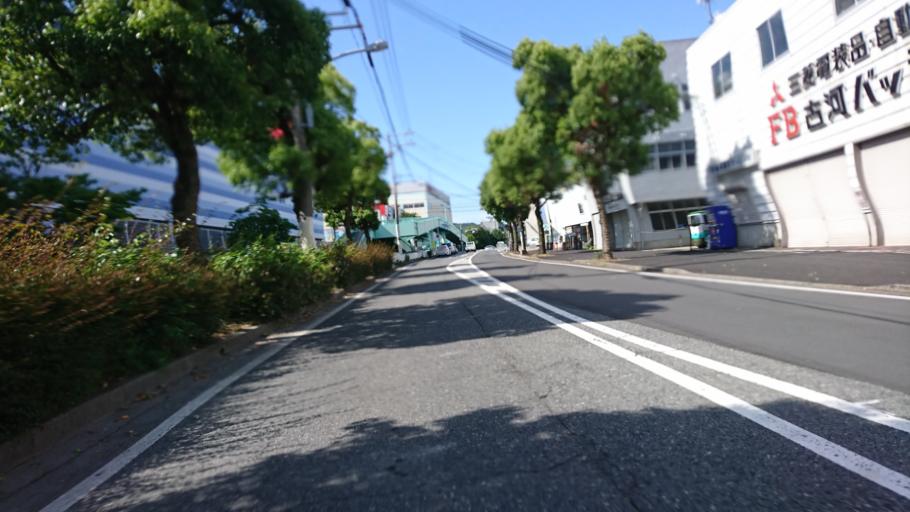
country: JP
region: Hyogo
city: Himeji
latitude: 34.8287
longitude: 134.7153
